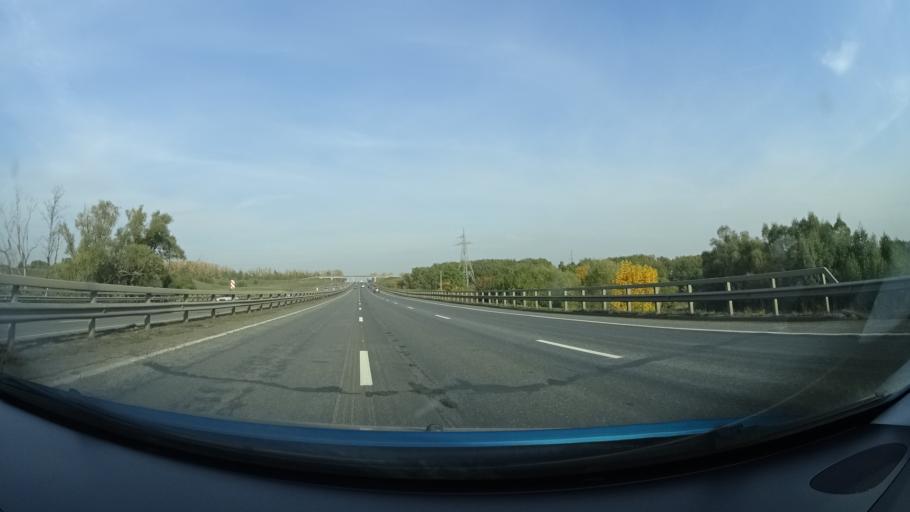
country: RU
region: Bashkortostan
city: Avdon
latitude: 54.6670
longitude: 55.7478
